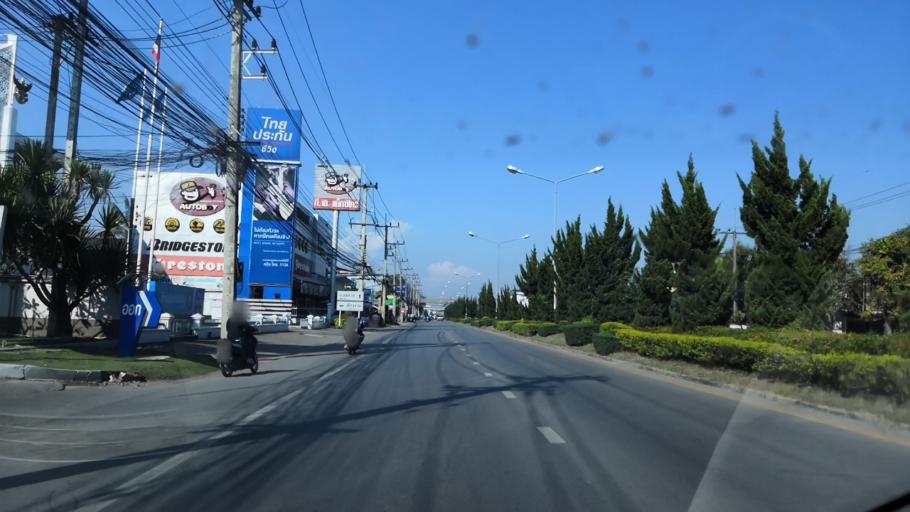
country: TH
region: Chiang Rai
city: Chiang Rai
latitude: 19.9315
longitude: 99.8446
